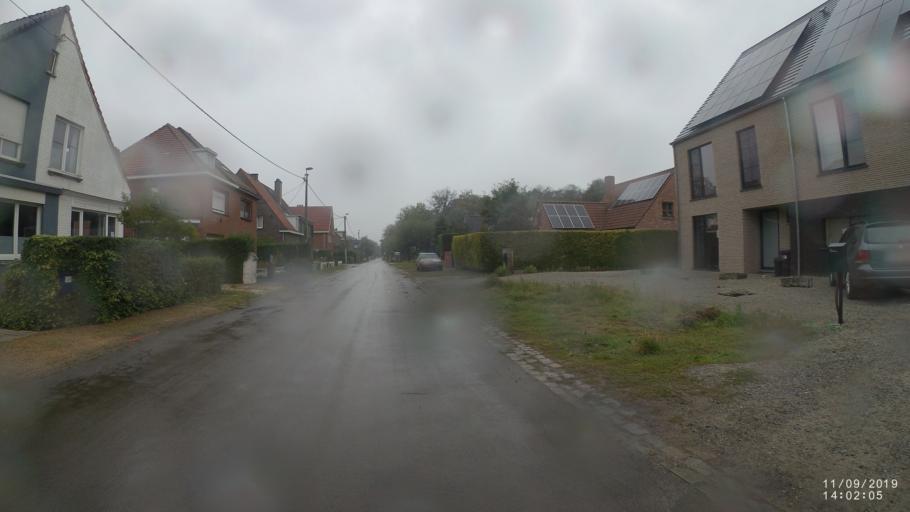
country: BE
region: Flanders
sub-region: Provincie Oost-Vlaanderen
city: Evergem
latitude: 51.0796
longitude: 3.6960
